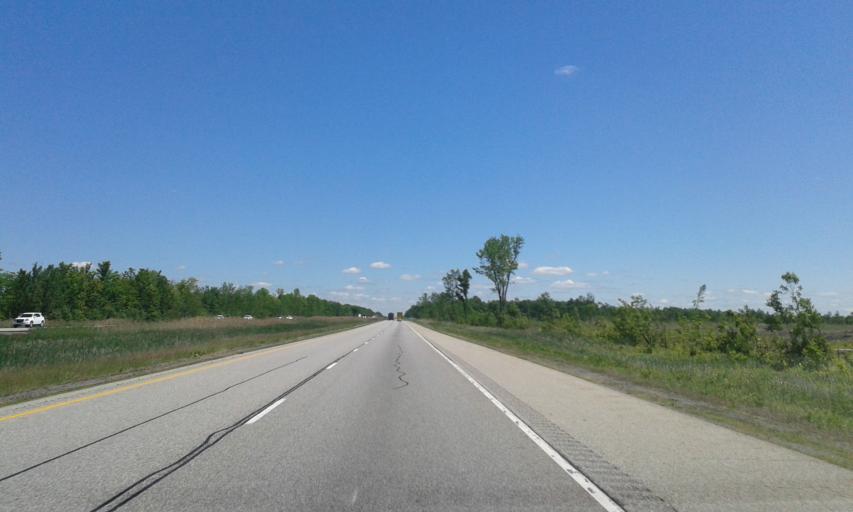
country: US
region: New York
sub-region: St. Lawrence County
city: Norfolk
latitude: 44.8974
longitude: -75.2439
